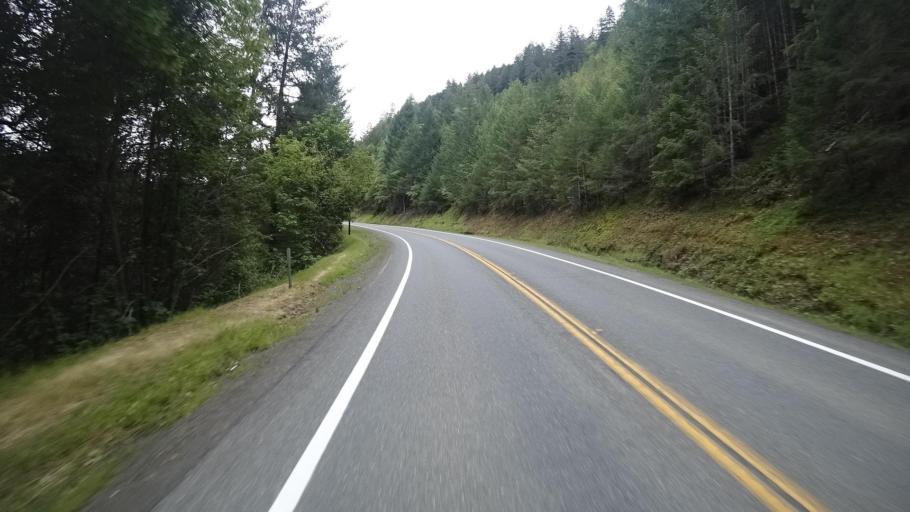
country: US
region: California
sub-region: Humboldt County
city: Willow Creek
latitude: 40.9984
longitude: -123.6409
